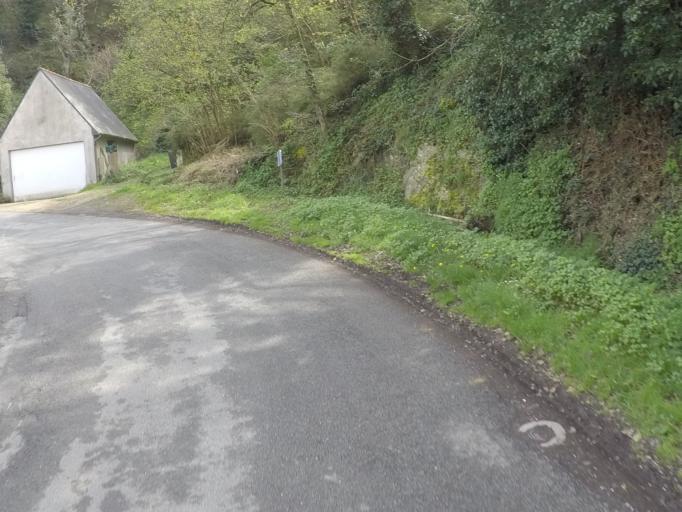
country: FR
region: Brittany
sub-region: Departement des Cotes-d'Armor
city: Plouezec
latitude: 48.7261
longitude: -2.9527
